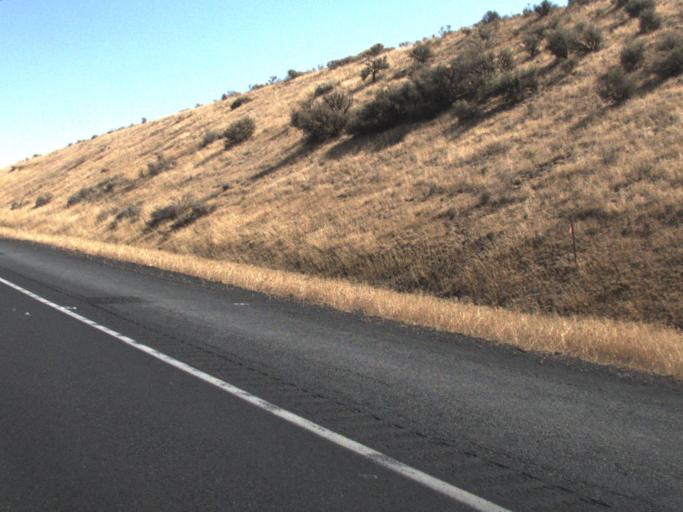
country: US
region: Washington
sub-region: Grant County
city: Warden
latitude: 47.0868
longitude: -118.8637
